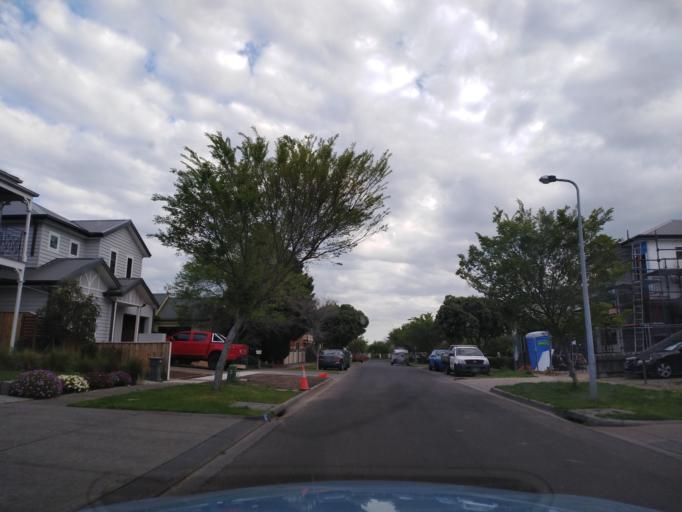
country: AU
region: Victoria
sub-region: Hobsons Bay
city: Williamstown North
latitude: -37.8574
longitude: 144.8764
